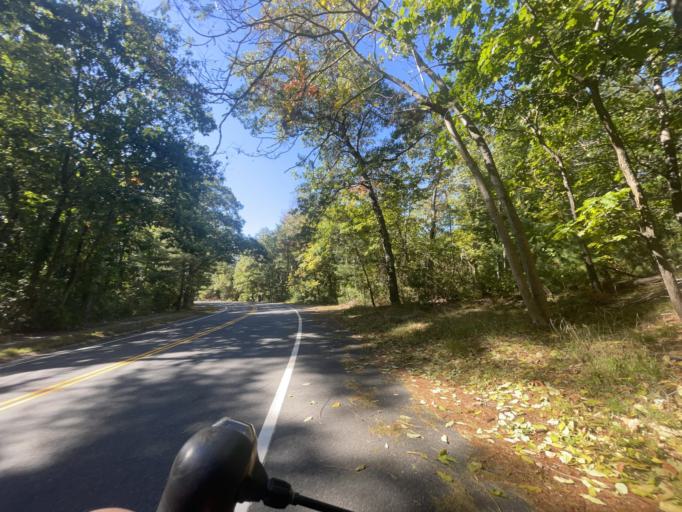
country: US
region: Massachusetts
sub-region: Norfolk County
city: Milton
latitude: 42.2359
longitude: -71.0348
